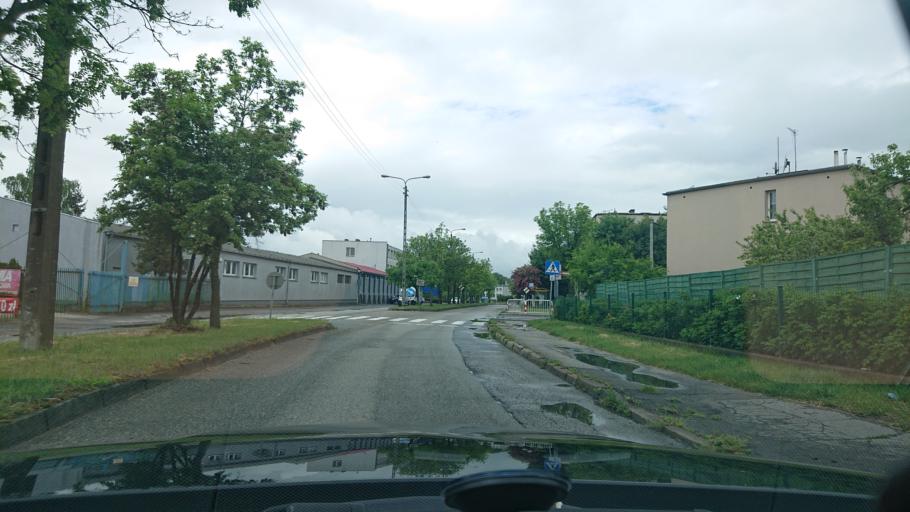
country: PL
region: Greater Poland Voivodeship
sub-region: Powiat gnieznienski
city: Gniezno
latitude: 52.5330
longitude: 17.6241
